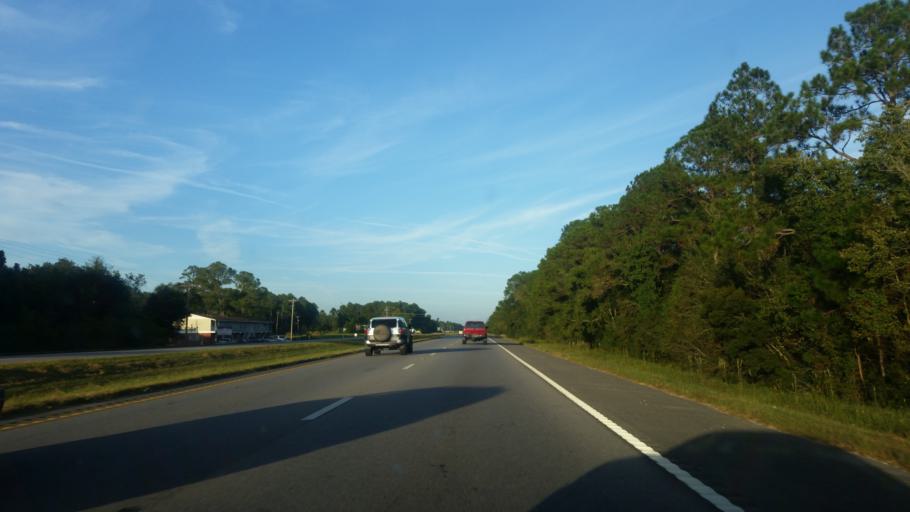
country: US
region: Mississippi
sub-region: Jackson County
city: Moss Point
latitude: 30.4038
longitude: -88.4861
